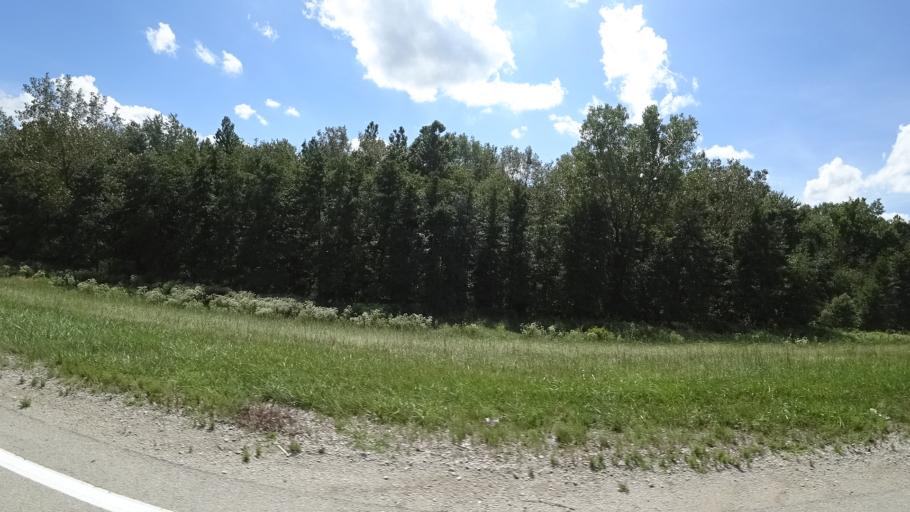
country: US
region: Illinois
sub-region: Cook County
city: Tinley Park
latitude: 41.5570
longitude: -87.7612
